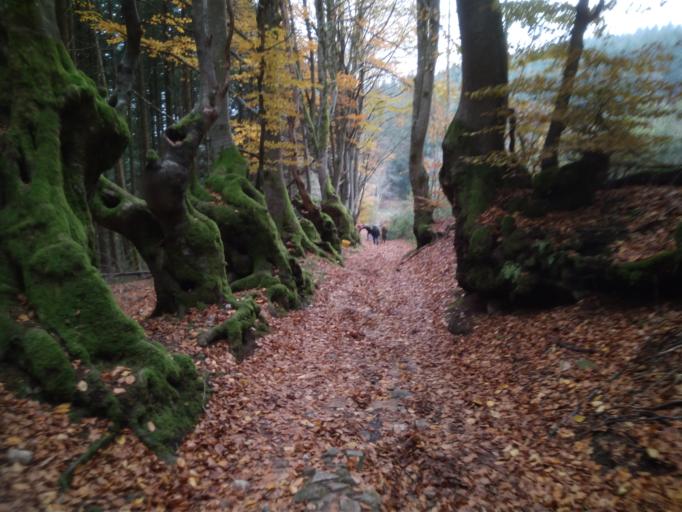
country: FR
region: Auvergne
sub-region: Departement de l'Allier
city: Le Mayet-de-Montagne
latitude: 46.0495
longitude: 3.7746
